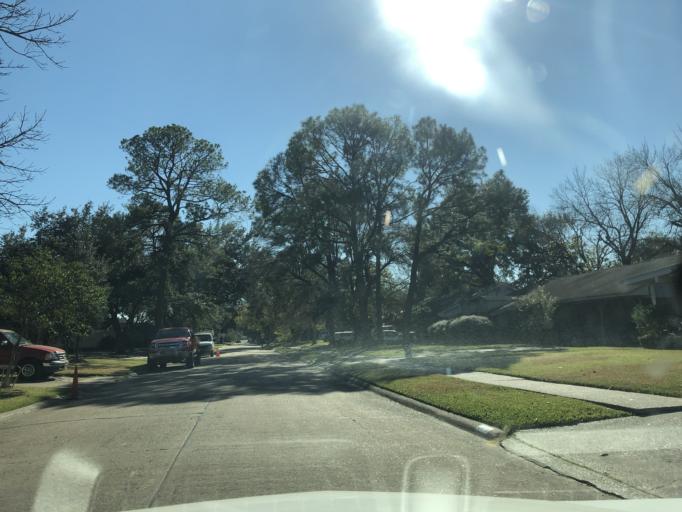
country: US
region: Texas
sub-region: Harris County
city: Bellaire
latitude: 29.6831
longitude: -95.5037
